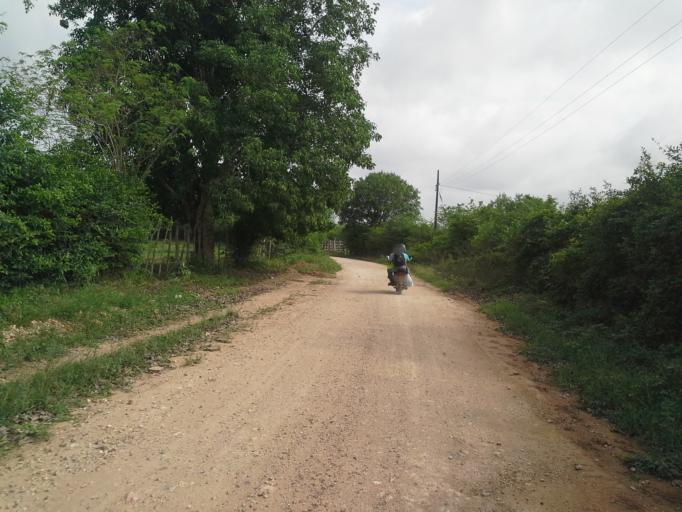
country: CO
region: Cordoba
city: Chima
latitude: 9.1713
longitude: -75.6123
